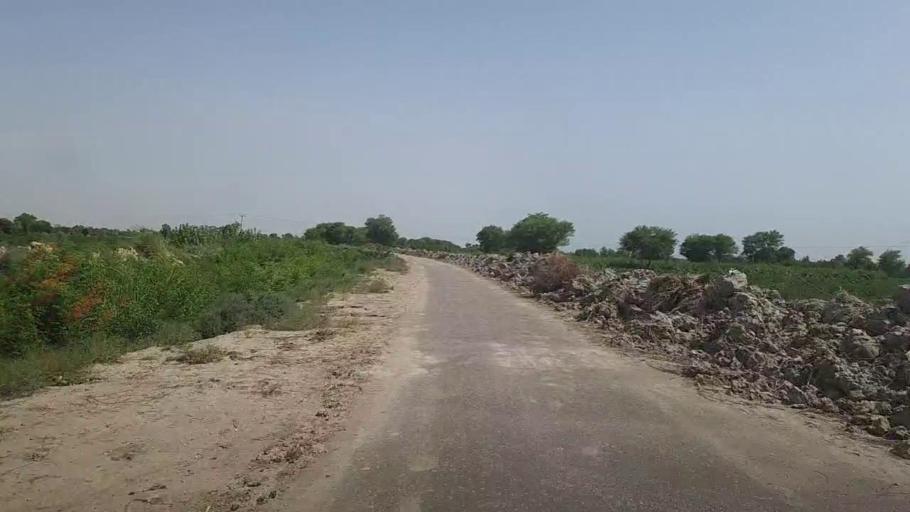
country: PK
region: Sindh
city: Pad Idan
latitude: 26.8136
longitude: 68.3278
